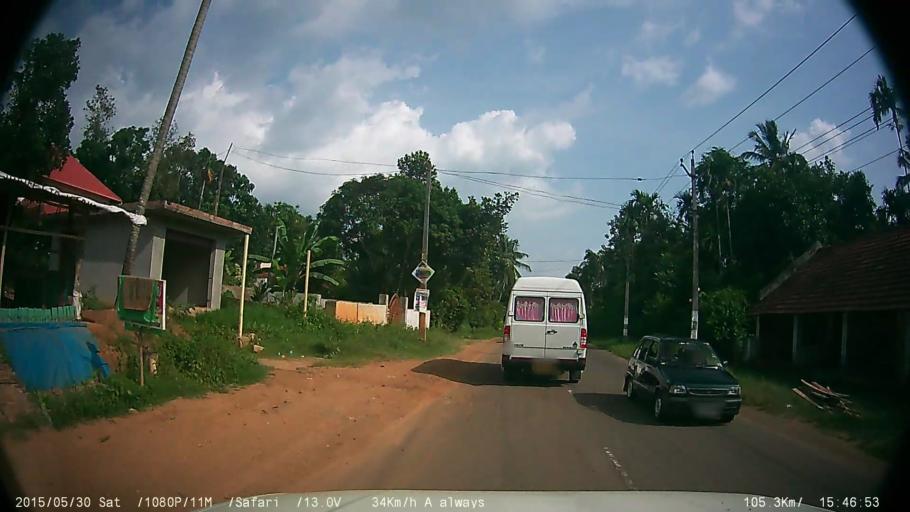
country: IN
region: Kerala
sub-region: Wayanad
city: Panamaram
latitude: 11.7078
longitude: 76.0784
